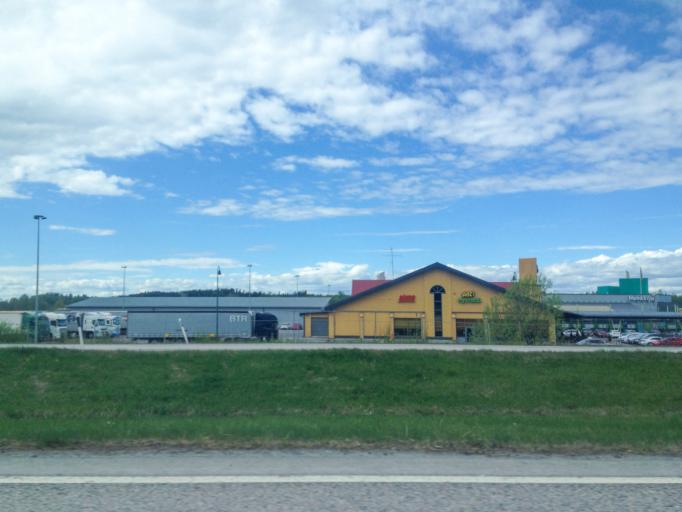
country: FI
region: Uusimaa
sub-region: Helsinki
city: Hyvinge
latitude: 60.6178
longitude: 24.8083
